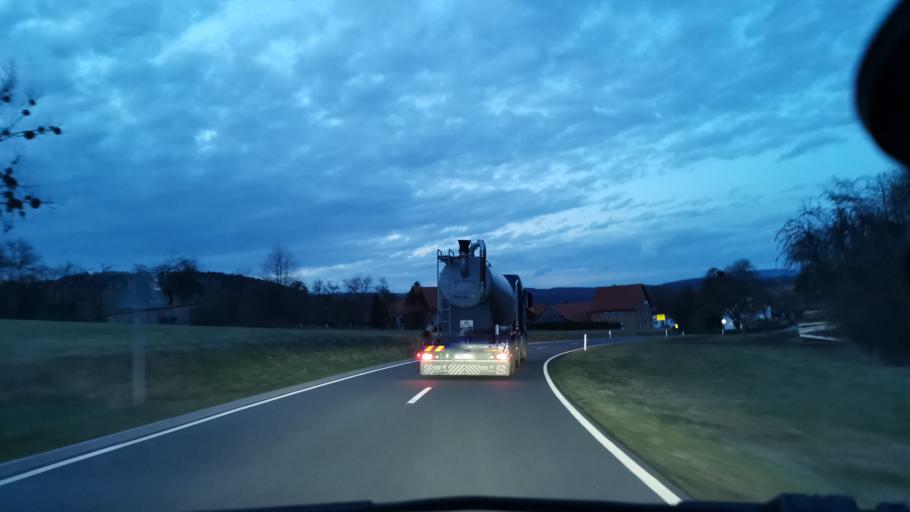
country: DE
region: Hesse
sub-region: Regierungsbezirk Kassel
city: Cornberg
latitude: 51.0945
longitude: 9.8120
